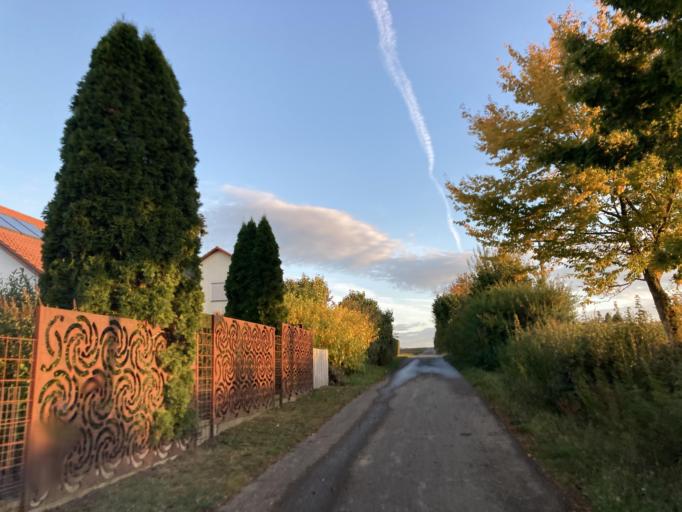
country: DE
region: Baden-Wuerttemberg
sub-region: Regierungsbezirk Stuttgart
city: Bondorf
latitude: 48.4887
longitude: 8.8002
